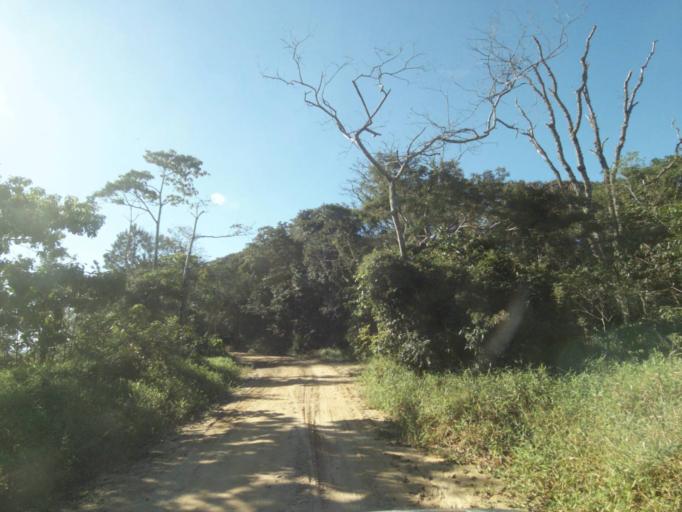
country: BR
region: Parana
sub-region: Tibagi
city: Tibagi
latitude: -24.5490
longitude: -50.4693
